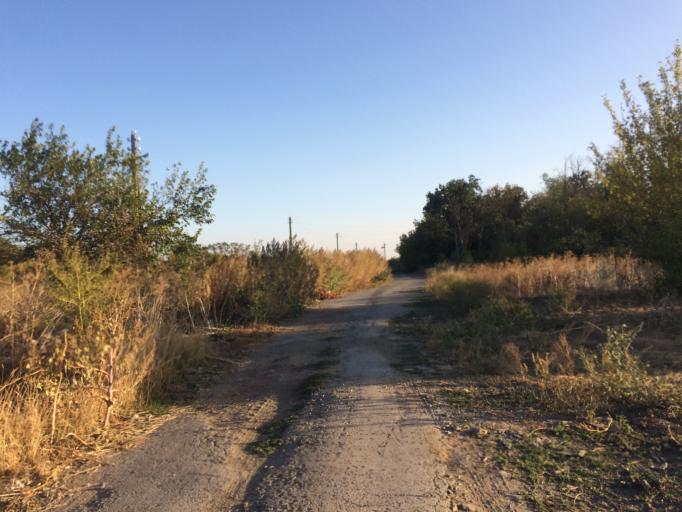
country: RU
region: Rostov
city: Gigant
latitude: 46.5190
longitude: 41.1948
